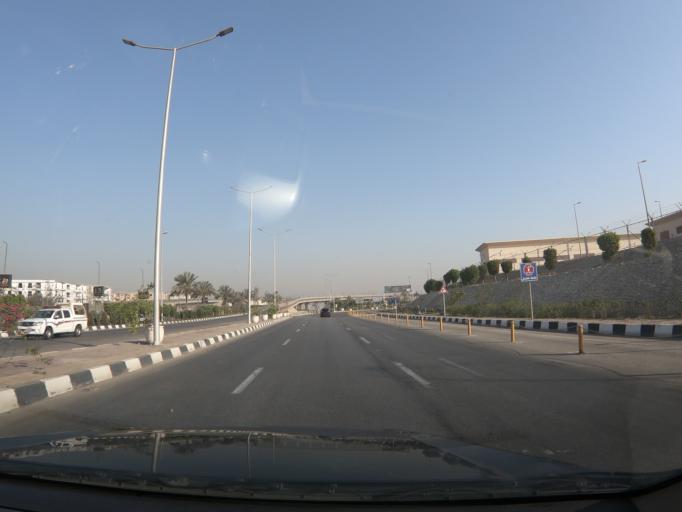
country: EG
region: Muhafazat al Qalyubiyah
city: Al Khankah
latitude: 30.1076
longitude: 31.3859
